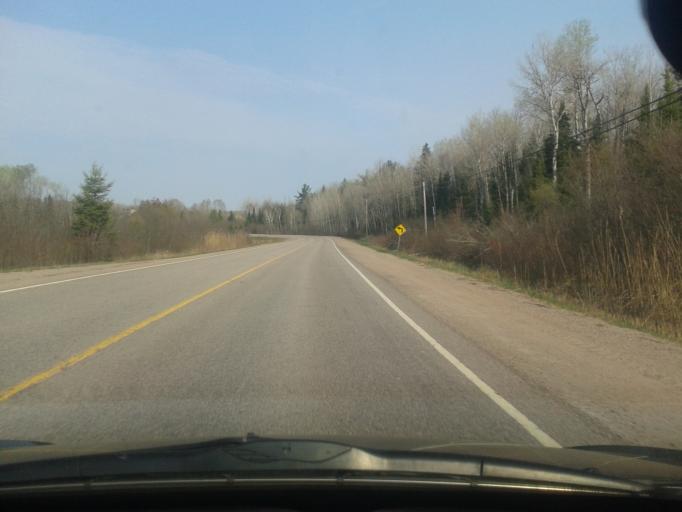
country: CA
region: Ontario
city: Powassan
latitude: 46.1936
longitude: -79.3198
